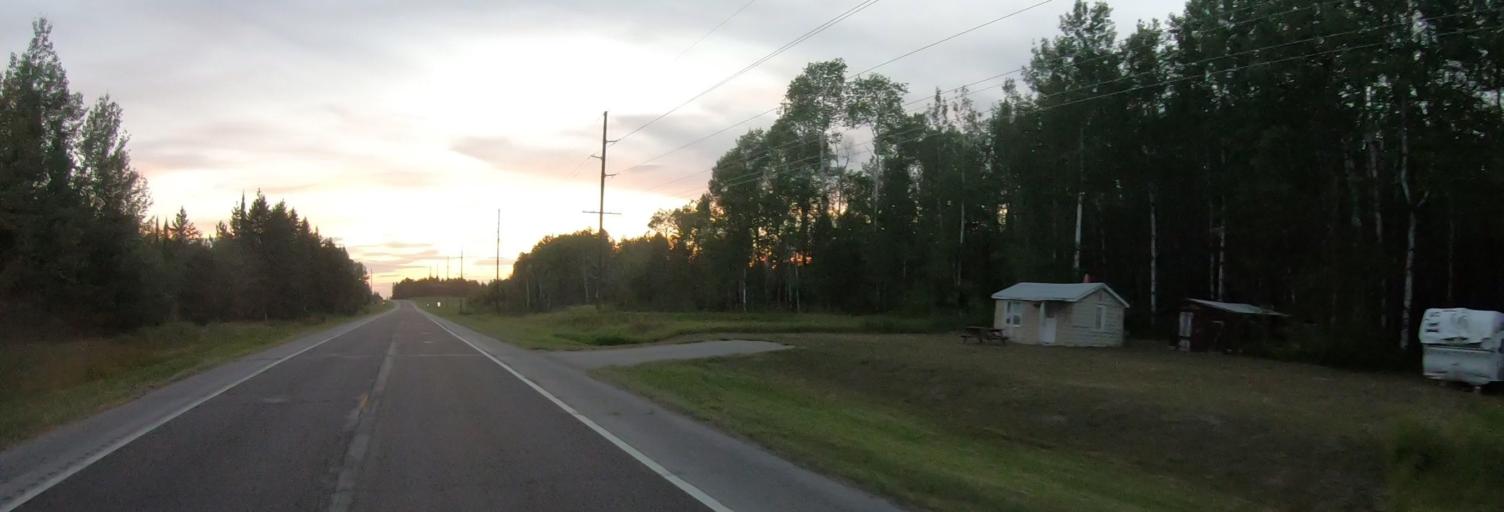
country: US
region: Minnesota
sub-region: Saint Louis County
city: Parkville
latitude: 47.8464
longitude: -92.5441
